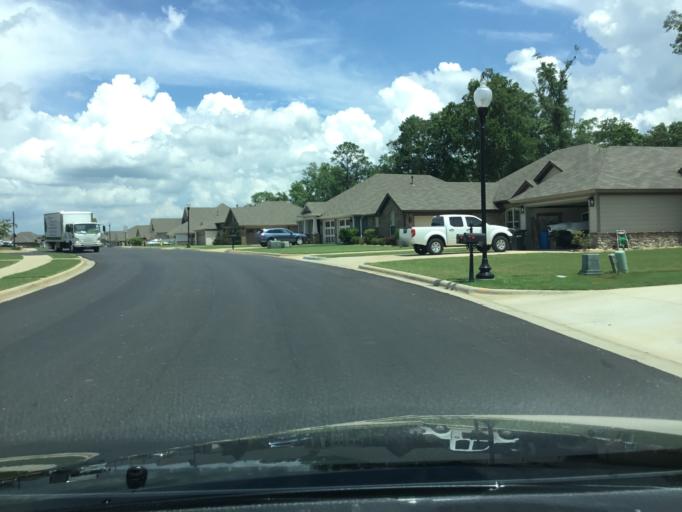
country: US
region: Alabama
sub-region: Montgomery County
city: Pike Road
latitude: 32.3362
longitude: -86.0793
